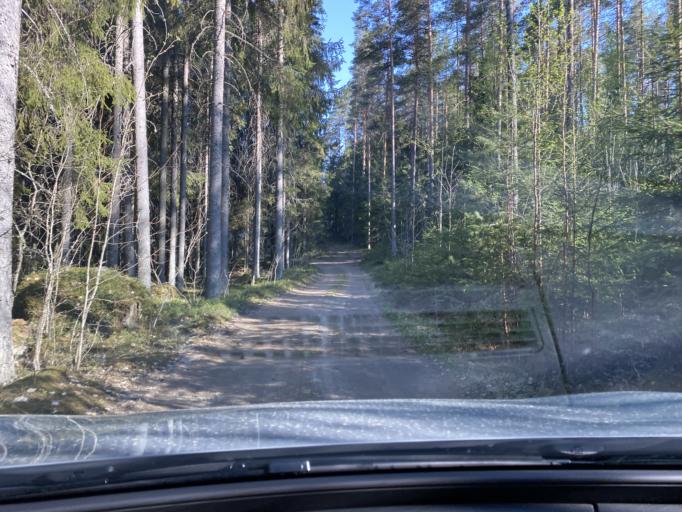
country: FI
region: Pirkanmaa
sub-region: Lounais-Pirkanmaa
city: Punkalaidun
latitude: 61.0155
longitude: 23.2000
